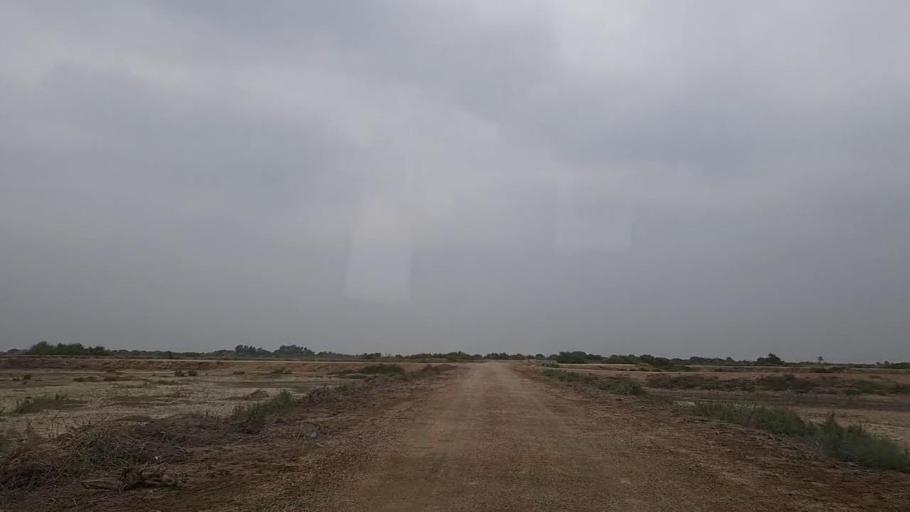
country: PK
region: Sindh
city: Mirpur Sakro
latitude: 24.6338
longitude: 67.7200
